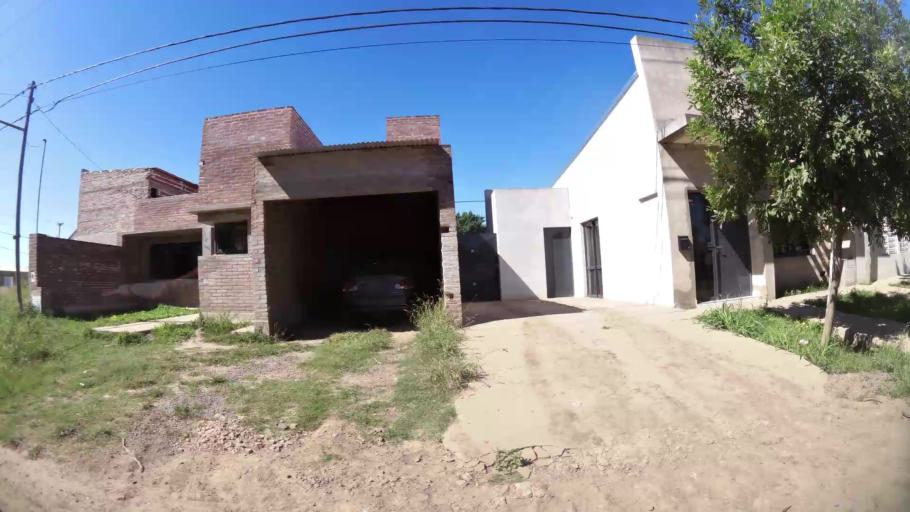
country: AR
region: Santa Fe
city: Esperanza
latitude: -31.4669
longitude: -60.9353
